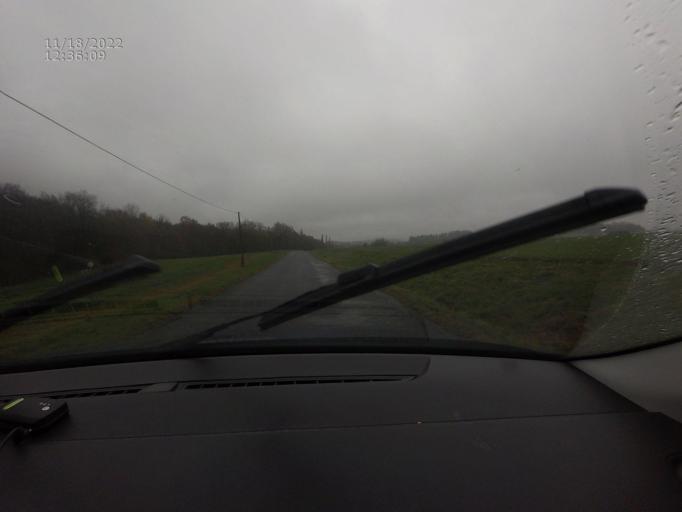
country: CZ
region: Plzensky
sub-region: Okres Klatovy
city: Planice
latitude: 49.4048
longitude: 13.5124
